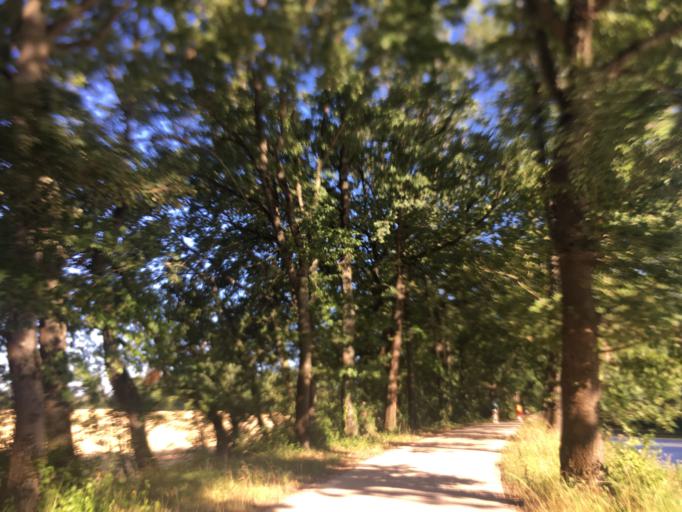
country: FR
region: Midi-Pyrenees
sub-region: Departement de la Haute-Garonne
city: Gardouch
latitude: 43.3971
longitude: 1.6830
